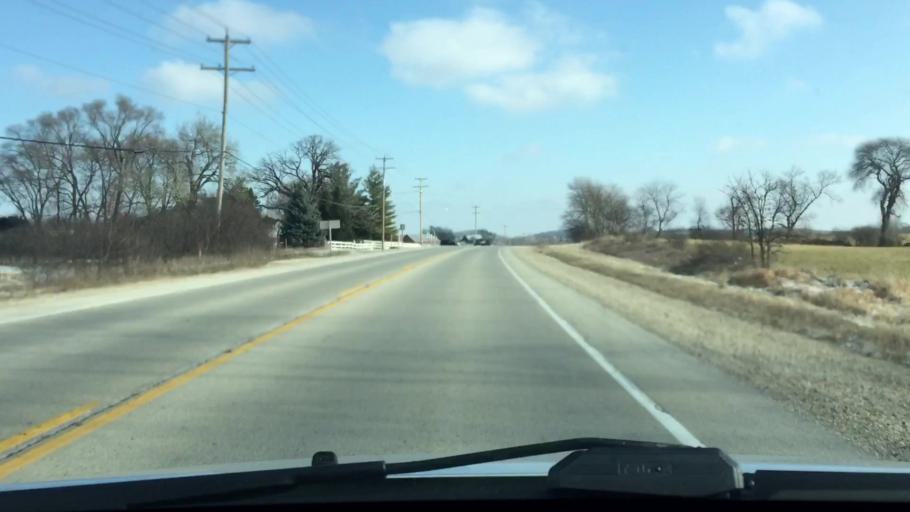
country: US
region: Wisconsin
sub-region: Waukesha County
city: Wales
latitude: 43.0182
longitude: -88.3661
